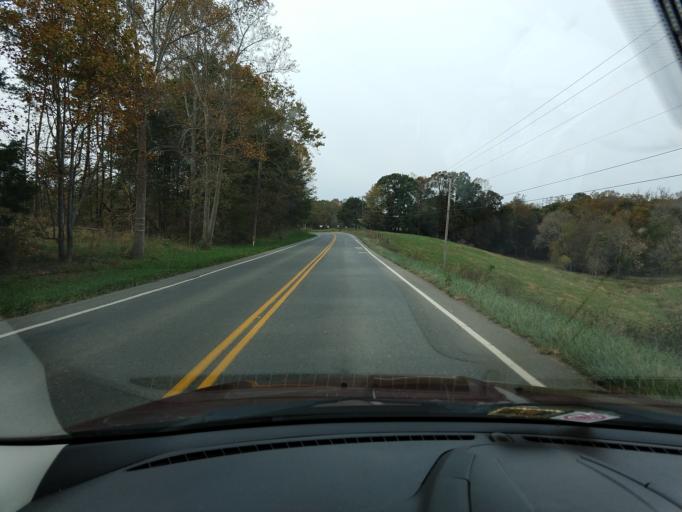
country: US
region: Virginia
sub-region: Franklin County
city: Union Hall
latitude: 36.9922
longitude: -79.7221
